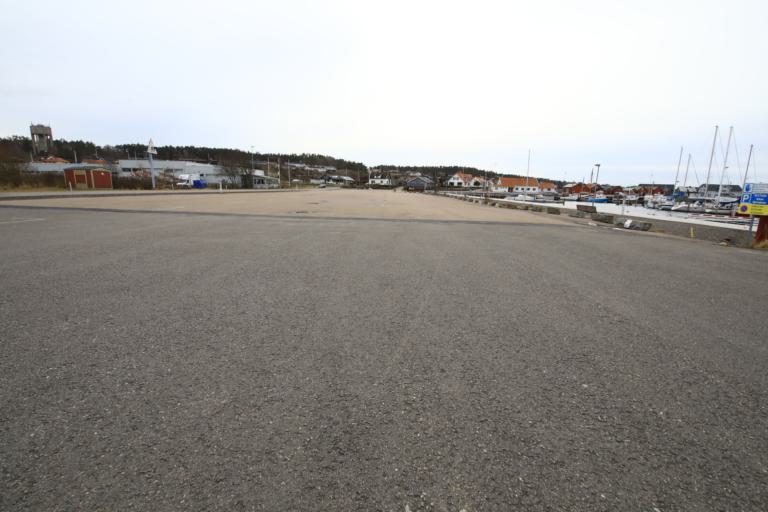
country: SE
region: Halland
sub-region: Kungsbacka Kommun
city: Frillesas
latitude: 57.2403
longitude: 12.1159
